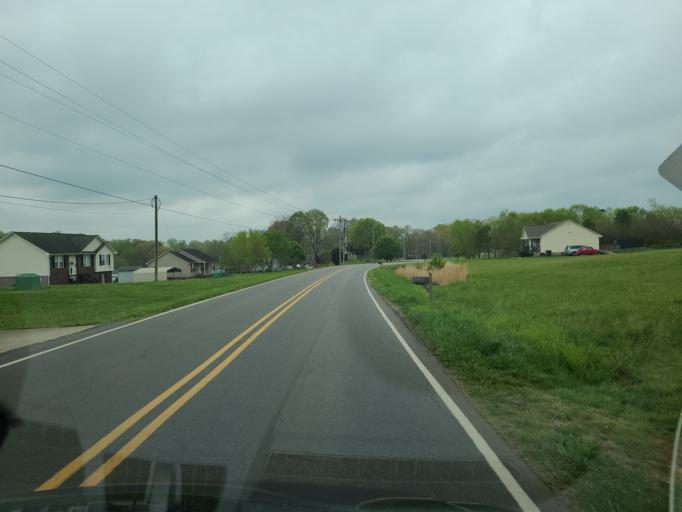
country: US
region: North Carolina
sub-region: Gaston County
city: Cherryville
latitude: 35.4475
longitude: -81.3651
